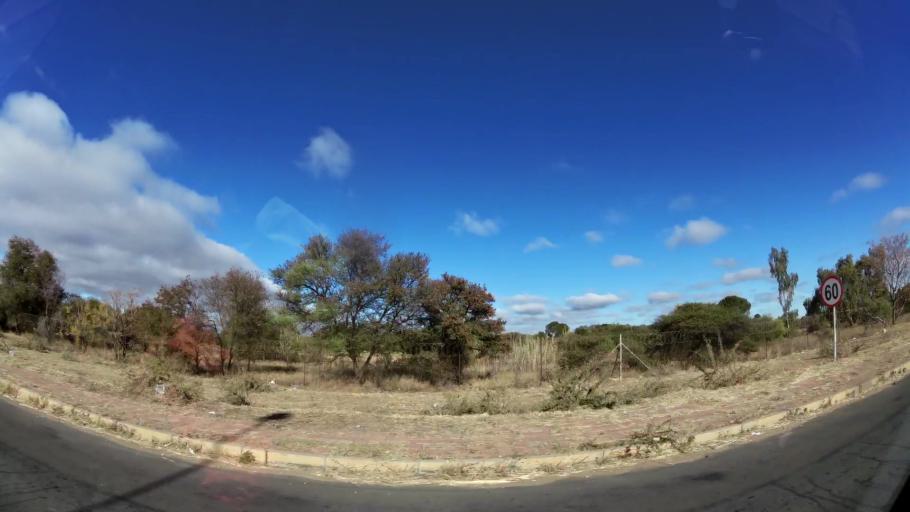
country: ZA
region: Limpopo
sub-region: Capricorn District Municipality
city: Polokwane
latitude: -23.9278
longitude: 29.4660
